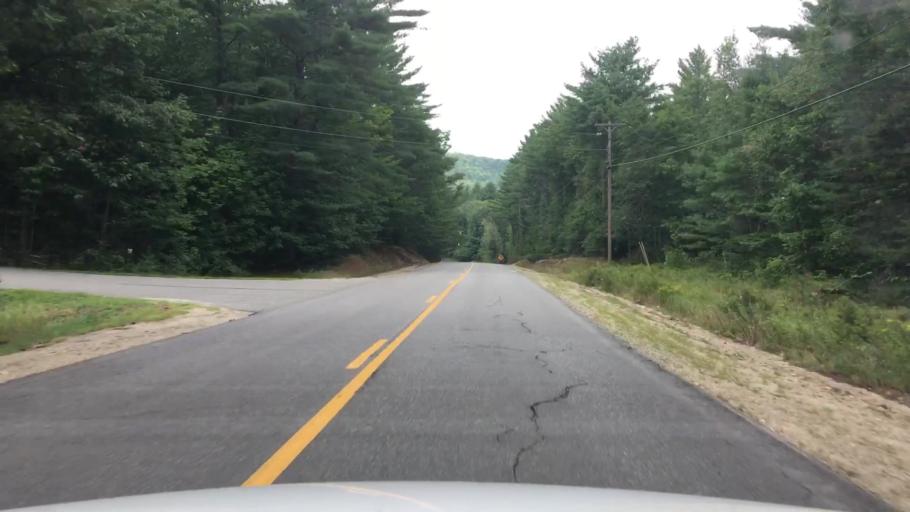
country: US
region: Maine
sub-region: Oxford County
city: Rumford
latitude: 44.5450
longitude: -70.6788
